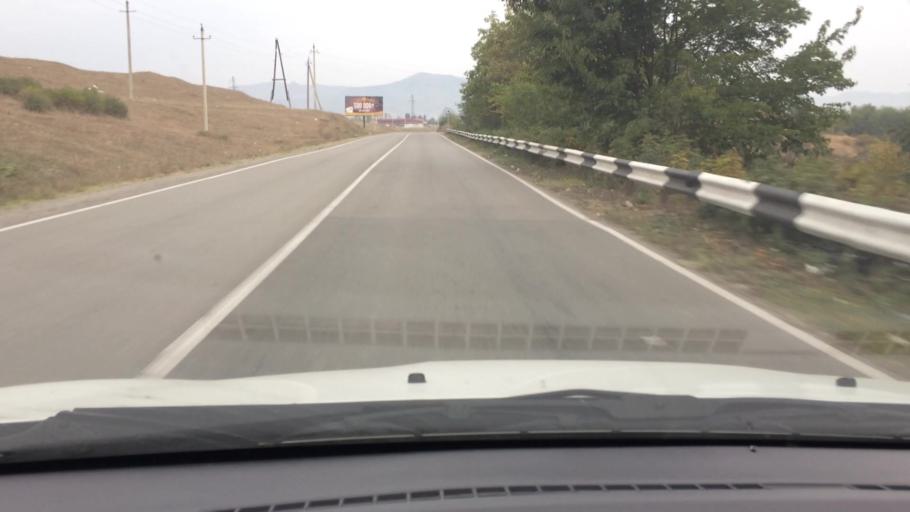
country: AM
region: Tavush
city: Bagratashen
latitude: 41.2296
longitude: 44.8228
